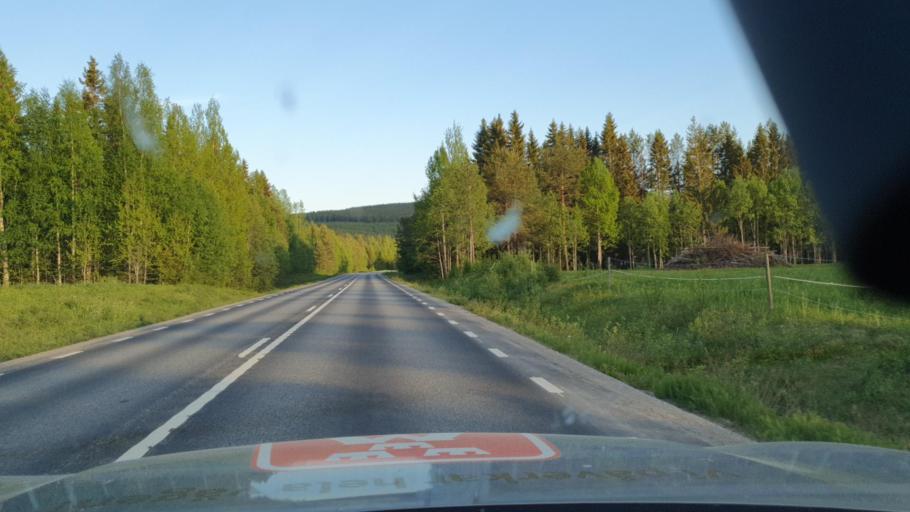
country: SE
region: Vaesternorrland
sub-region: Solleftea Kommun
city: As
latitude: 63.5534
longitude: 16.8423
